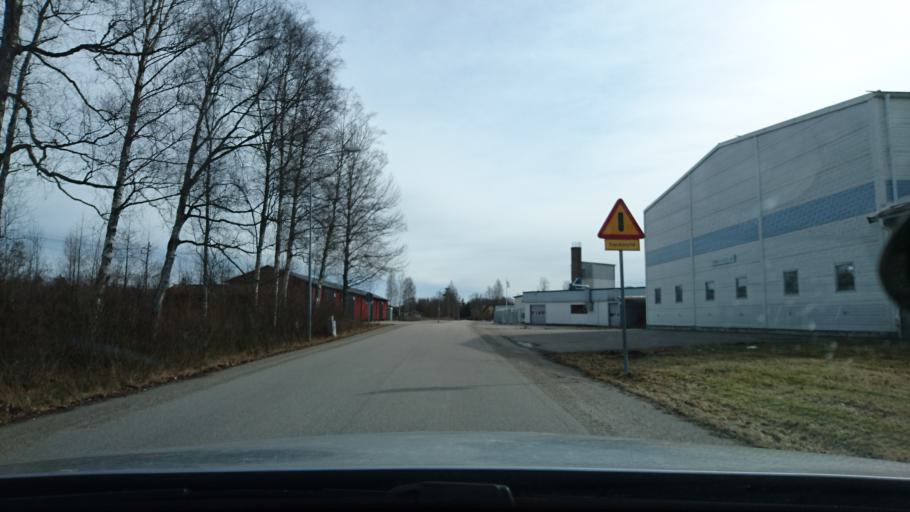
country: SE
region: Kronoberg
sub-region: Alvesta Kommun
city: Alvesta
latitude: 56.9185
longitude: 14.4515
